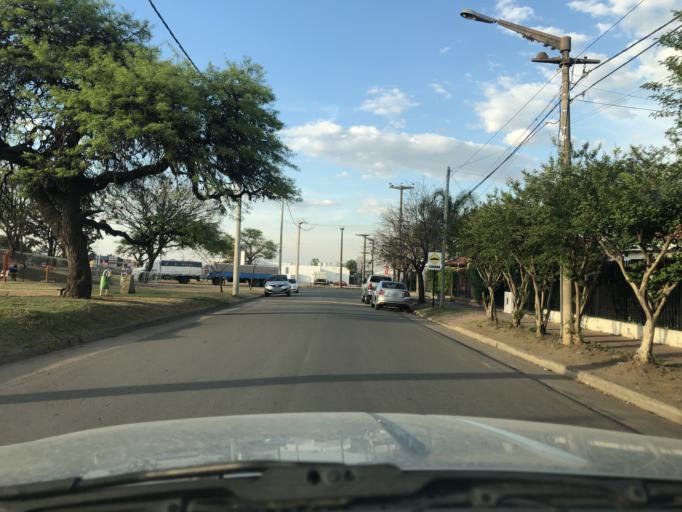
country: AR
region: Cordoba
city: Jesus Maria
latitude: -30.9795
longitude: -64.0850
